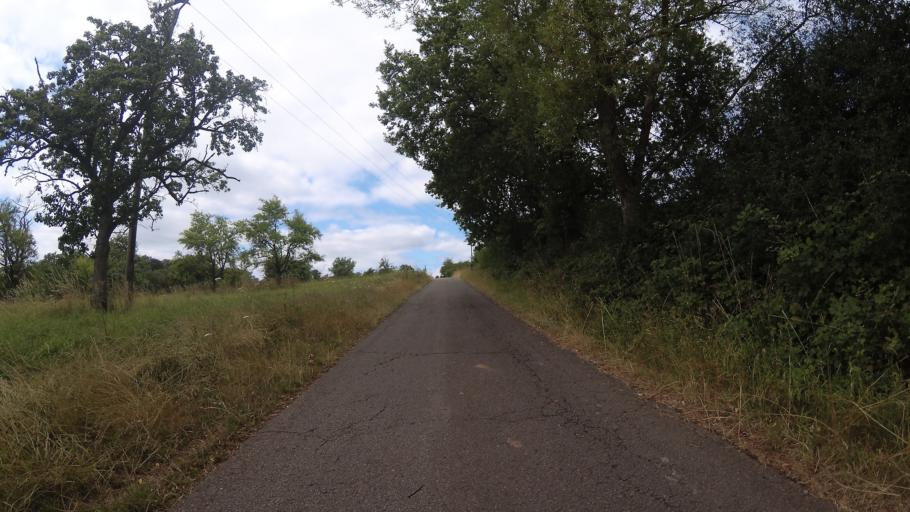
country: DE
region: Saarland
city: Mainzweiler
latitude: 49.4165
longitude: 7.1130
